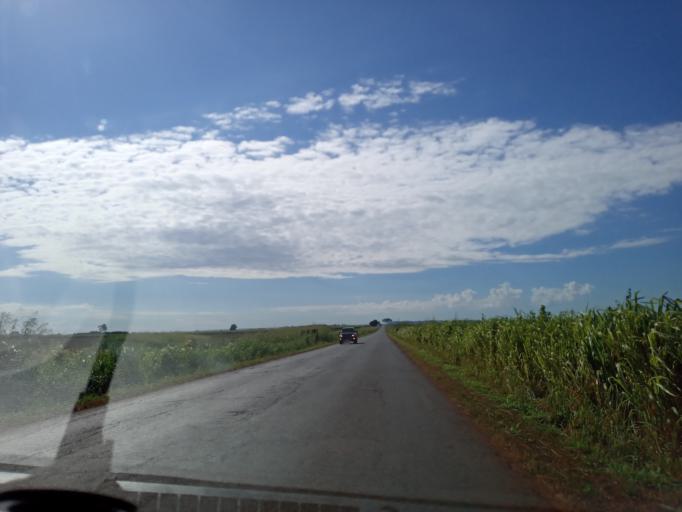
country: BR
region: Goias
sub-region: Itumbiara
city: Itumbiara
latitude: -18.4471
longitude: -49.1687
